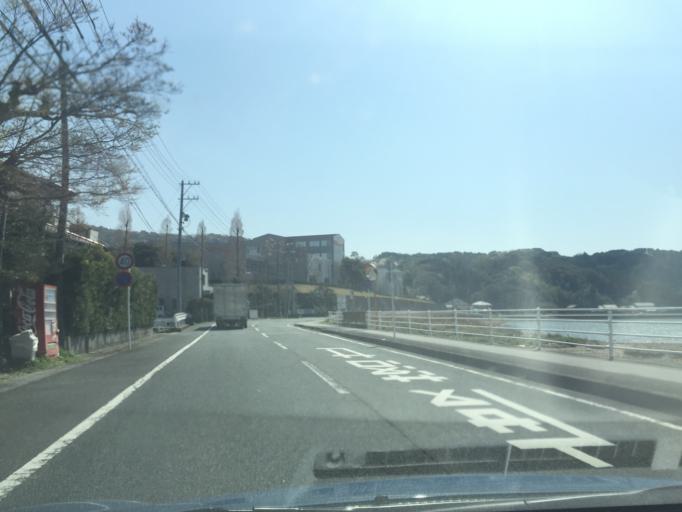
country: JP
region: Shizuoka
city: Hamamatsu
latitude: 34.7863
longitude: 137.6435
